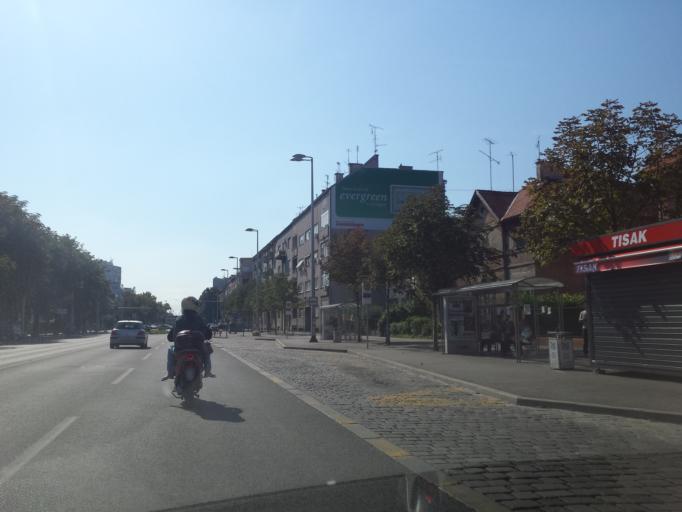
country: HR
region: Grad Zagreb
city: Zagreb
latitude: 45.8129
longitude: 15.9990
